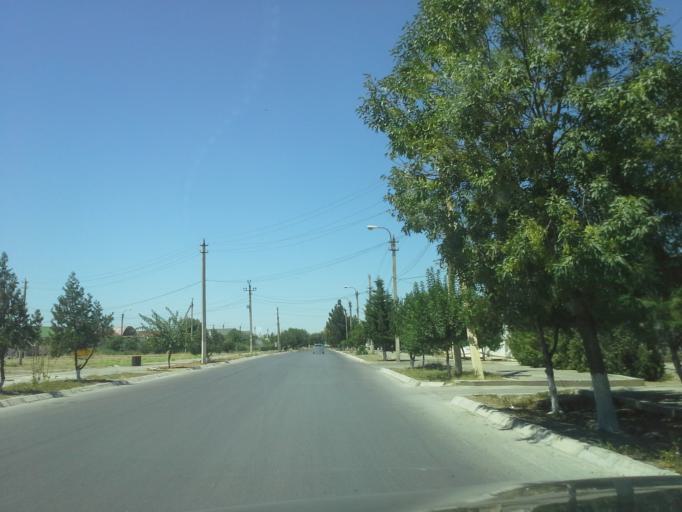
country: TM
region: Ahal
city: Abadan
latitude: 38.0298
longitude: 58.2693
